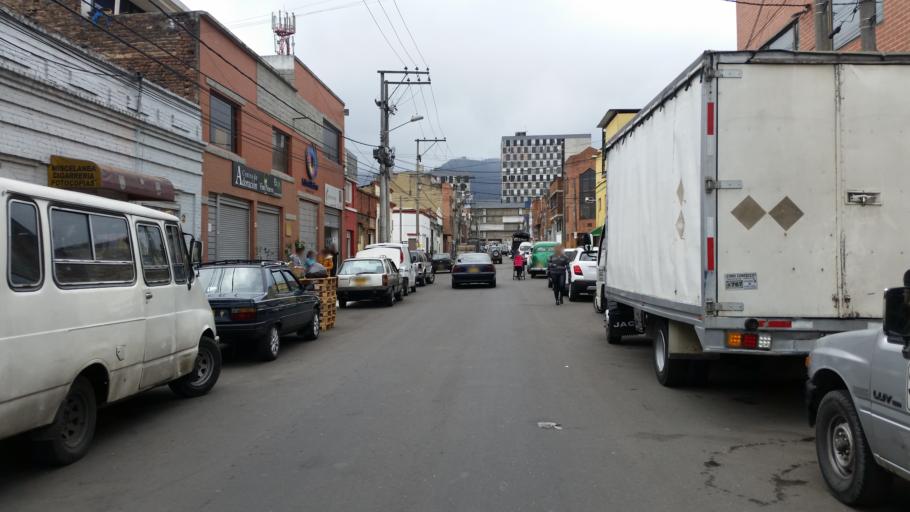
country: CO
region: Bogota D.C.
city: Bogota
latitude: 4.6221
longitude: -74.0902
